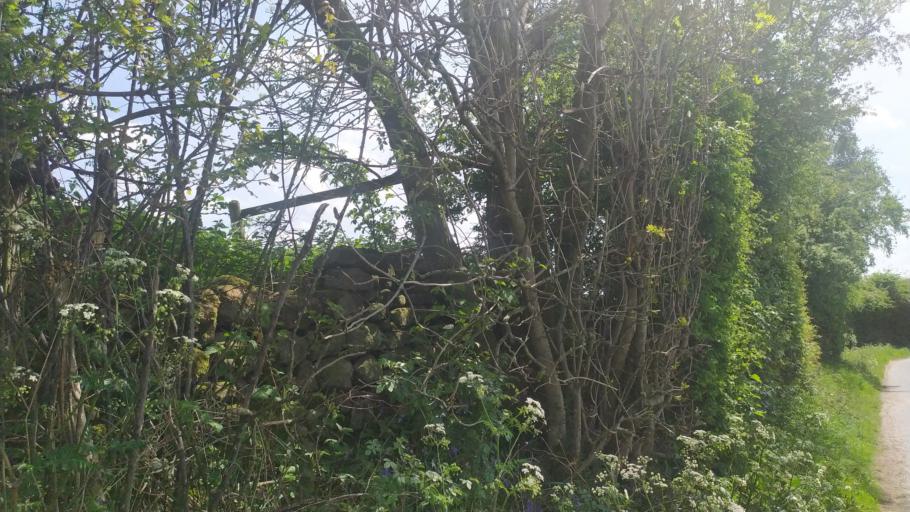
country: GB
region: England
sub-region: City and Borough of Leeds
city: Chapel Allerton
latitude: 53.8748
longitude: -1.5631
